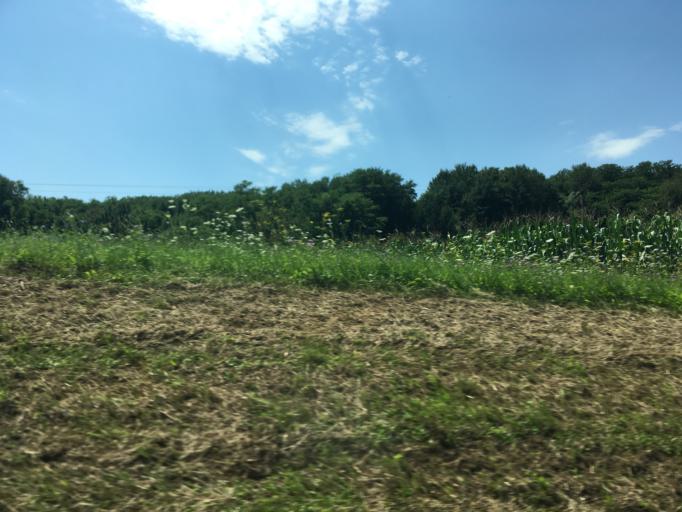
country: SI
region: Metlika
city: Metlika
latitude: 45.6045
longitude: 15.3326
